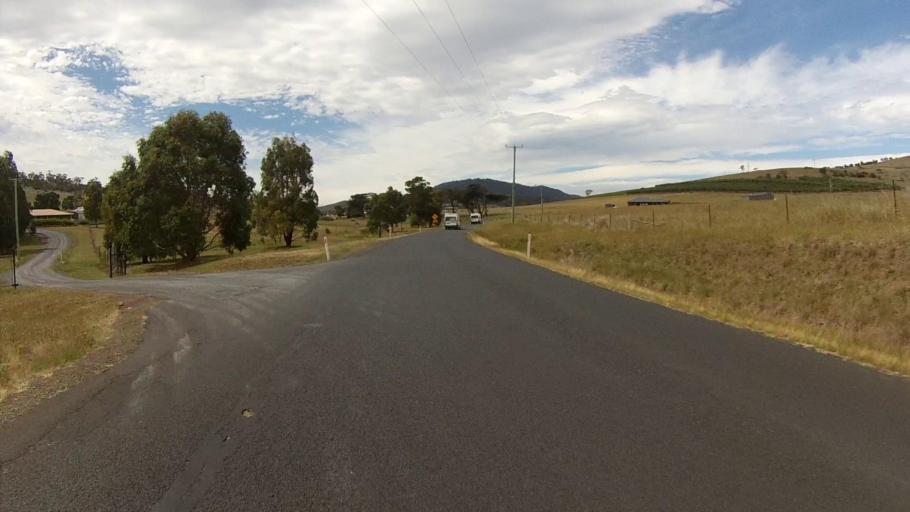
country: AU
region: Tasmania
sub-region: Brighton
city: Old Beach
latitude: -42.7045
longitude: 147.3122
